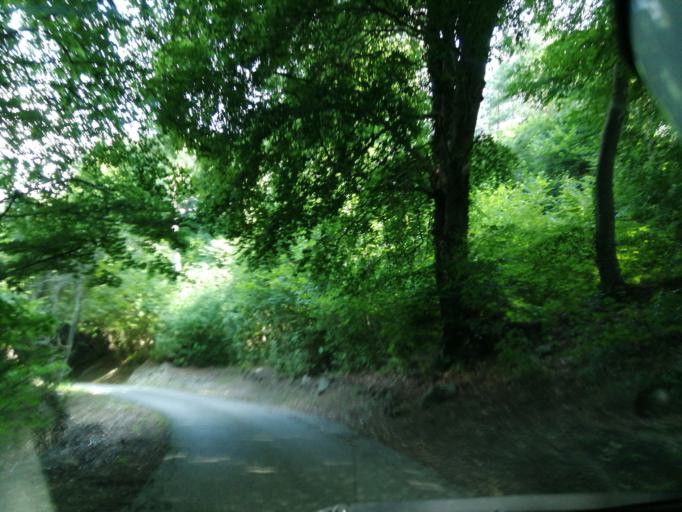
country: IT
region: Trentino-Alto Adige
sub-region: Provincia di Trento
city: Storo
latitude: 45.8280
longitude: 10.5703
